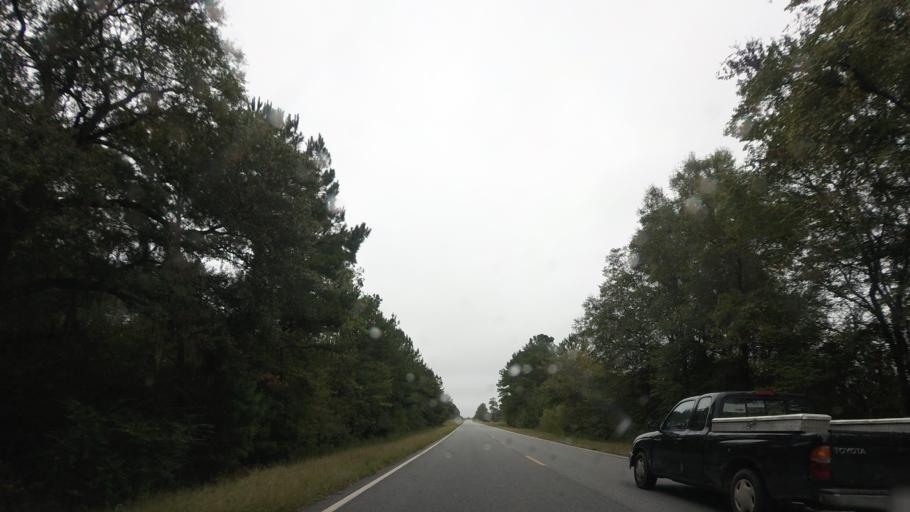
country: US
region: Georgia
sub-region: Berrien County
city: Enigma
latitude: 31.4372
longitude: -83.2414
